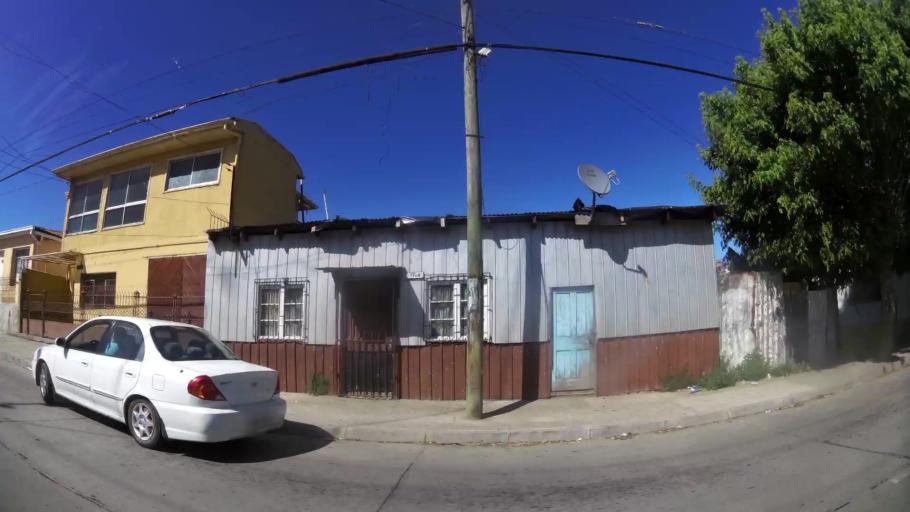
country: CL
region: Valparaiso
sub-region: Provincia de Valparaiso
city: Valparaiso
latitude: -33.0666
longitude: -71.5838
